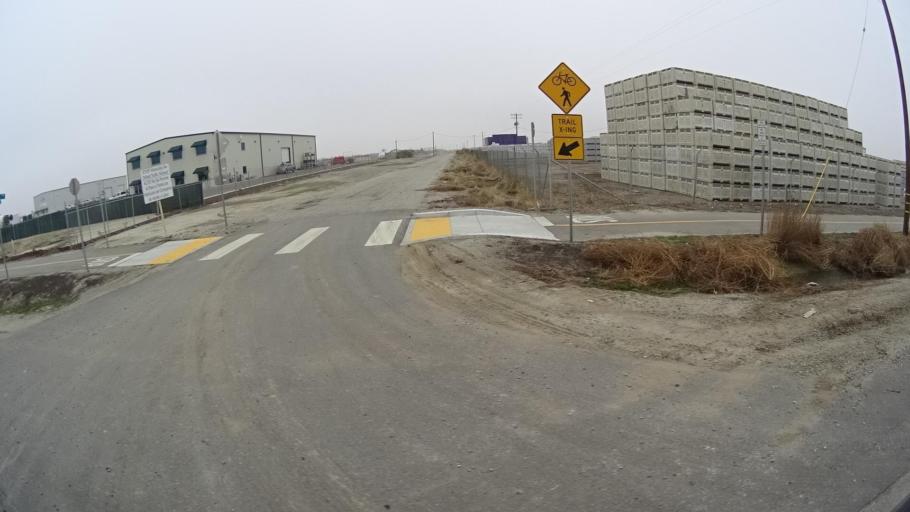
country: US
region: California
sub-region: Kern County
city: Rosedale
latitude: 35.2529
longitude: -119.2527
